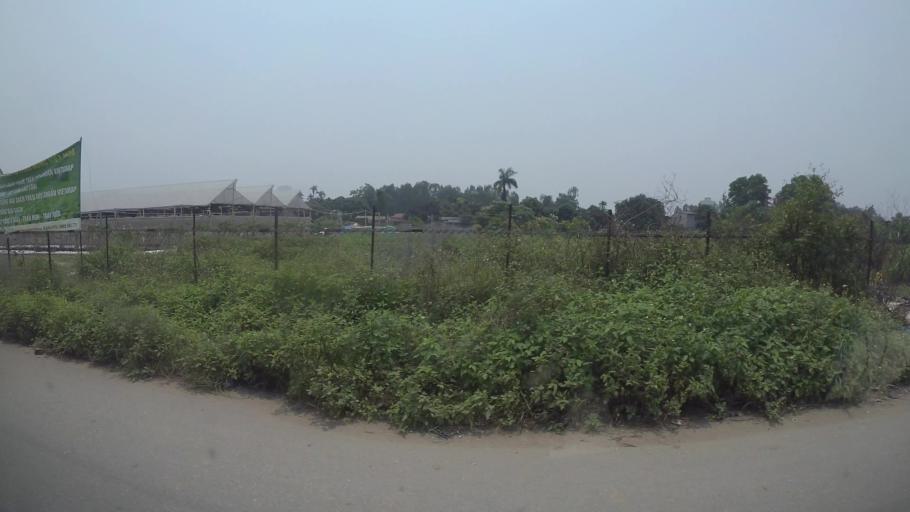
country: VN
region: Ha Noi
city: Ha Dong
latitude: 20.9977
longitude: 105.7668
